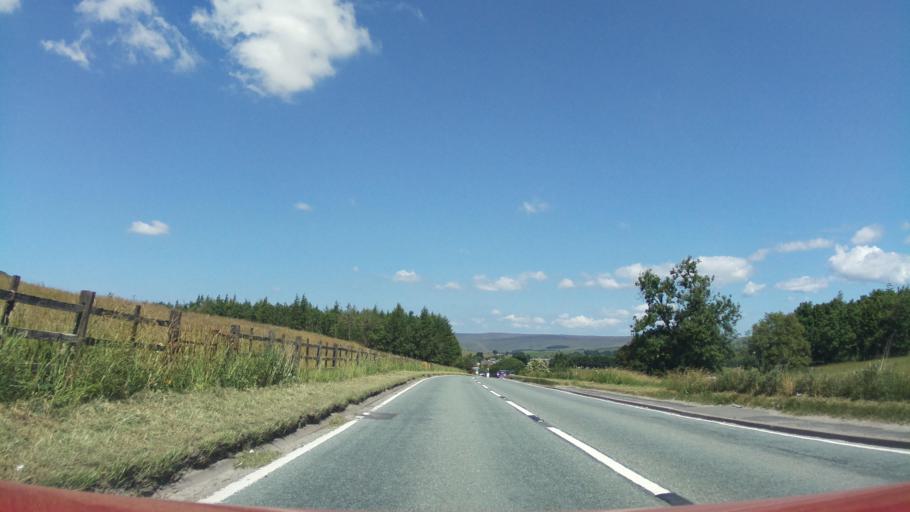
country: GB
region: England
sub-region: Derbyshire
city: Buxton
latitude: 53.2898
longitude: -1.8894
